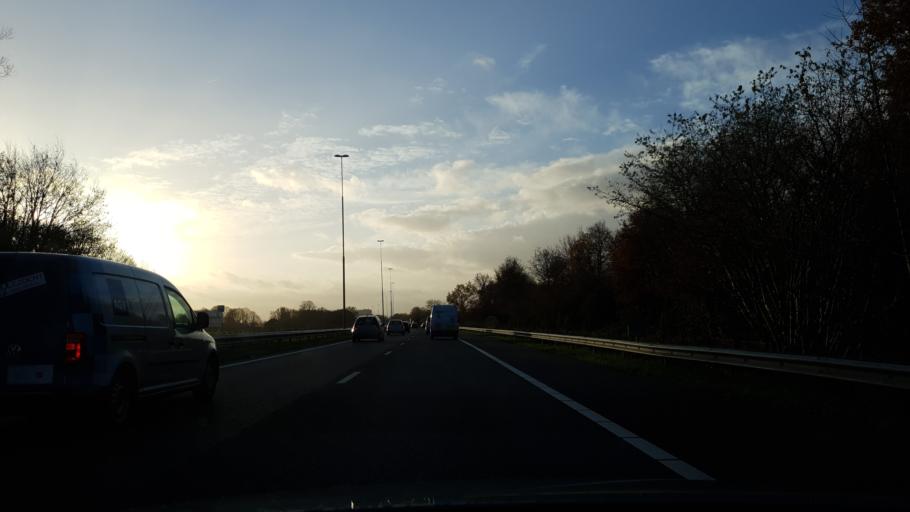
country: NL
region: North Brabant
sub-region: Gemeente Cuijk
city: Cuijk
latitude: 51.7131
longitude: 5.8712
